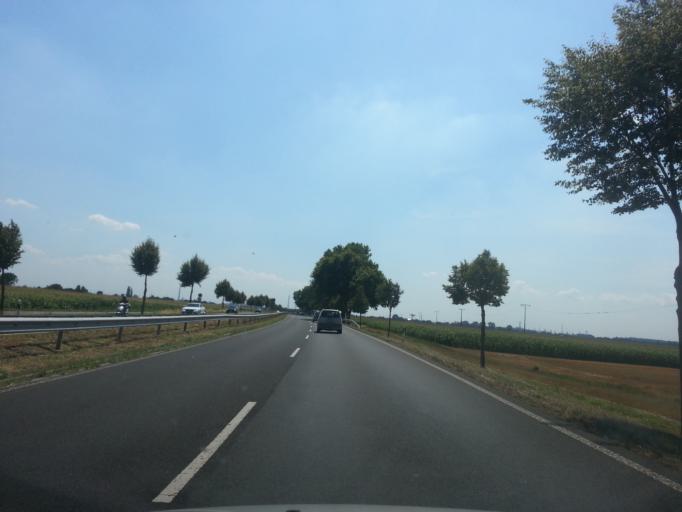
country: DE
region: Hesse
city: Lampertheim
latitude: 49.5772
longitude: 8.4470
